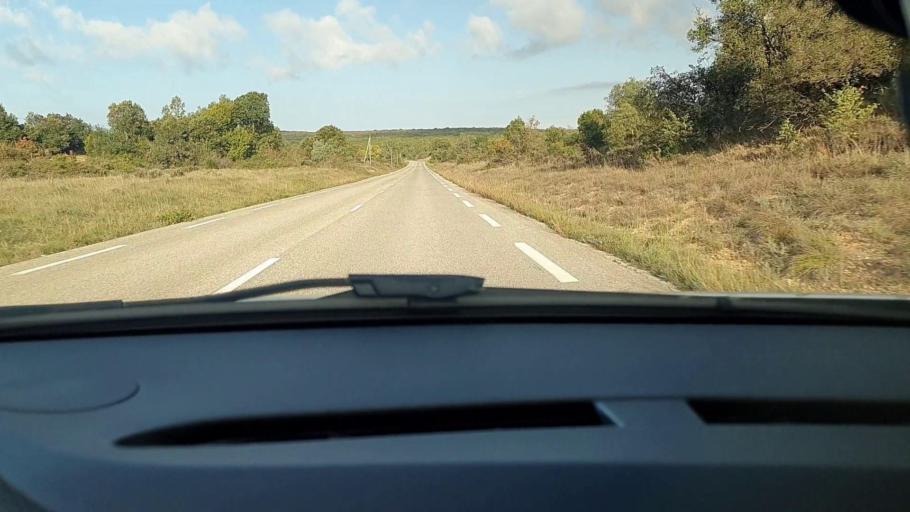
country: FR
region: Languedoc-Roussillon
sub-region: Departement du Gard
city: Barjac
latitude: 44.2143
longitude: 4.3329
